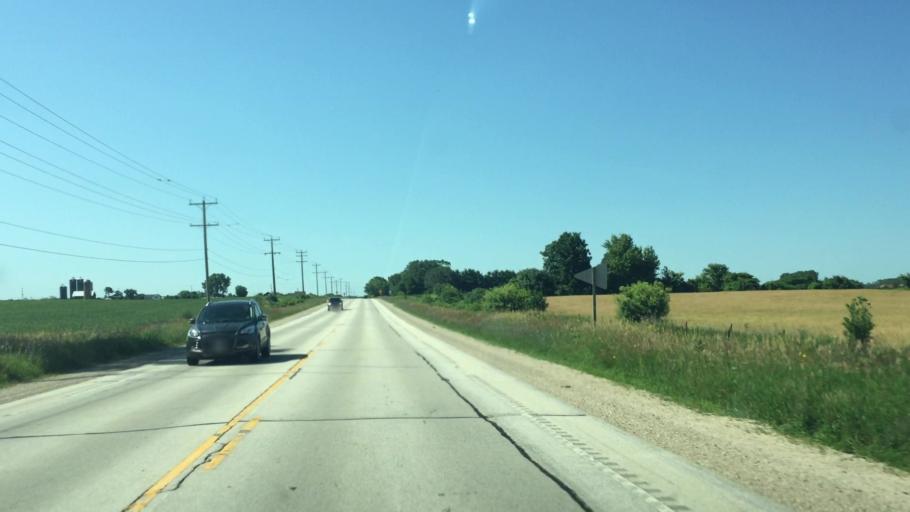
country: US
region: Wisconsin
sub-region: Calumet County
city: Sherwood
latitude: 44.1484
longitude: -88.2648
